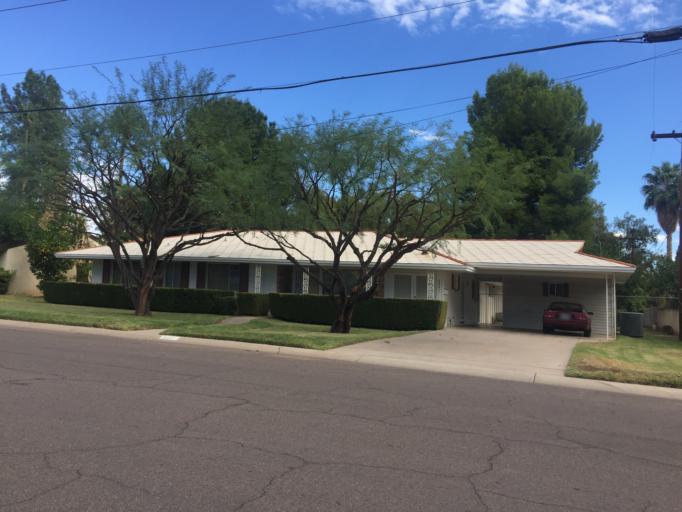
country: US
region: Arizona
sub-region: Maricopa County
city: Phoenix
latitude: 33.5316
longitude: -112.0694
